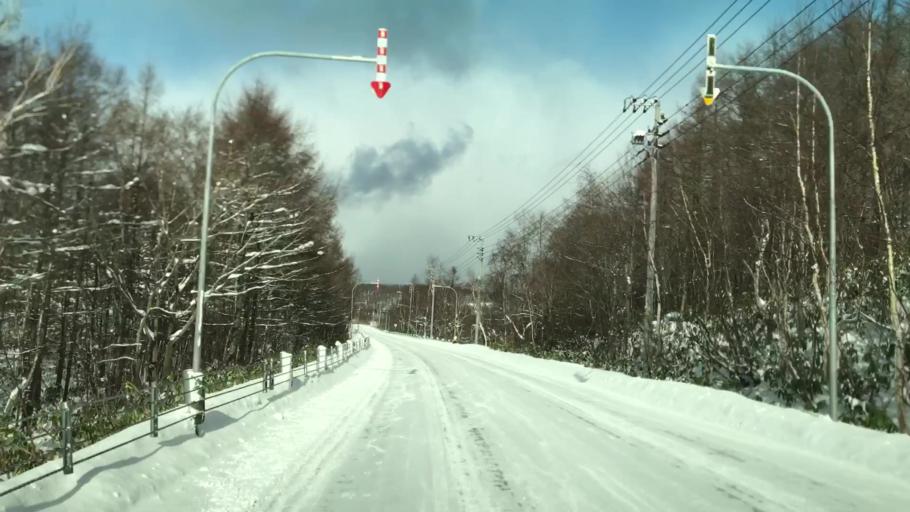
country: JP
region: Hokkaido
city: Yoichi
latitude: 43.2993
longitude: 140.5671
